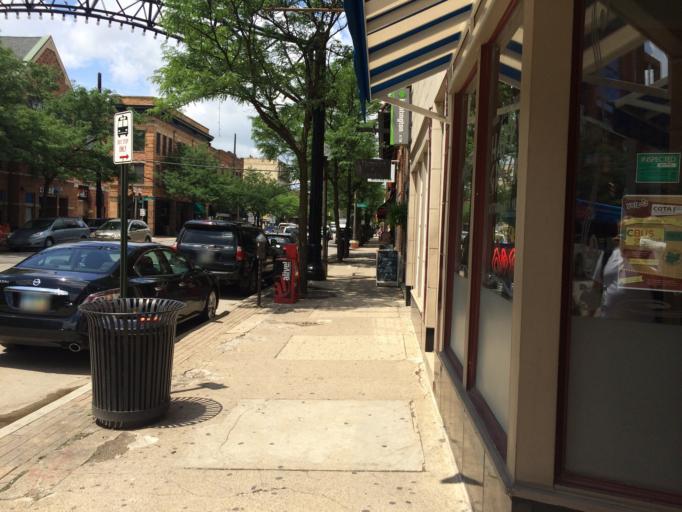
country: US
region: Ohio
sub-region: Franklin County
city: Columbus
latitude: 39.9757
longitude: -83.0032
